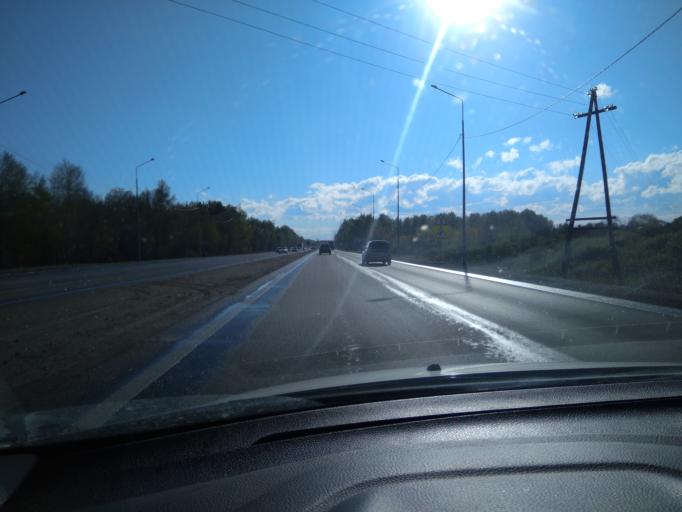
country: RU
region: Tjumen
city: Moskovskiy
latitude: 57.1170
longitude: 65.4290
